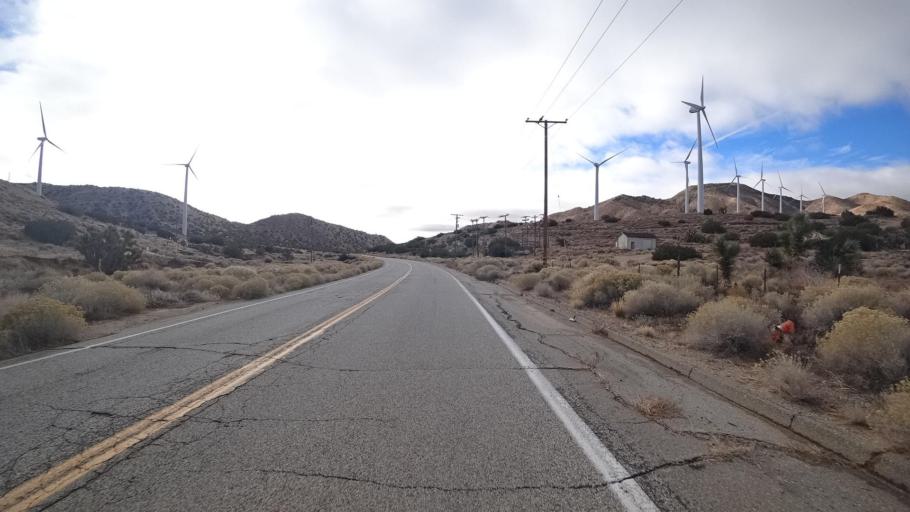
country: US
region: California
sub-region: Kern County
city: Tehachapi
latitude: 35.0282
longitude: -118.3524
